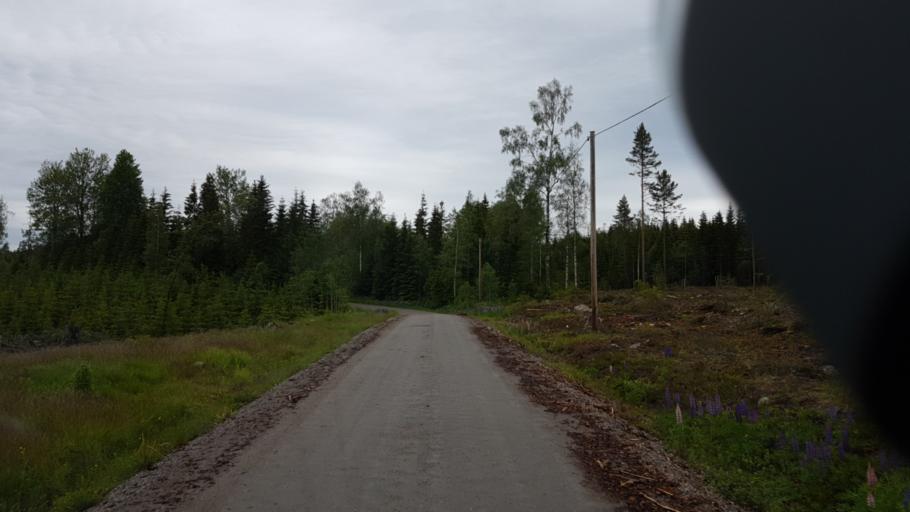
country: NO
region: Ostfold
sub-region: Romskog
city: Romskog
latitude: 59.7036
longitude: 12.0537
